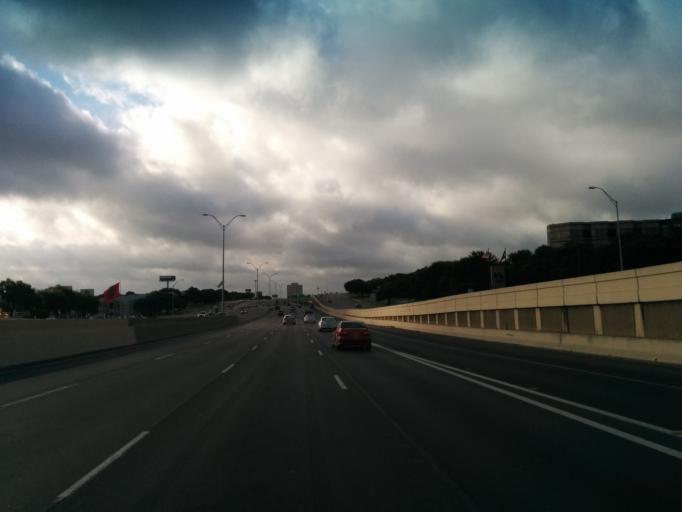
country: US
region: Texas
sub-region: Bexar County
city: Shavano Park
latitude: 29.5428
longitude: -98.5762
